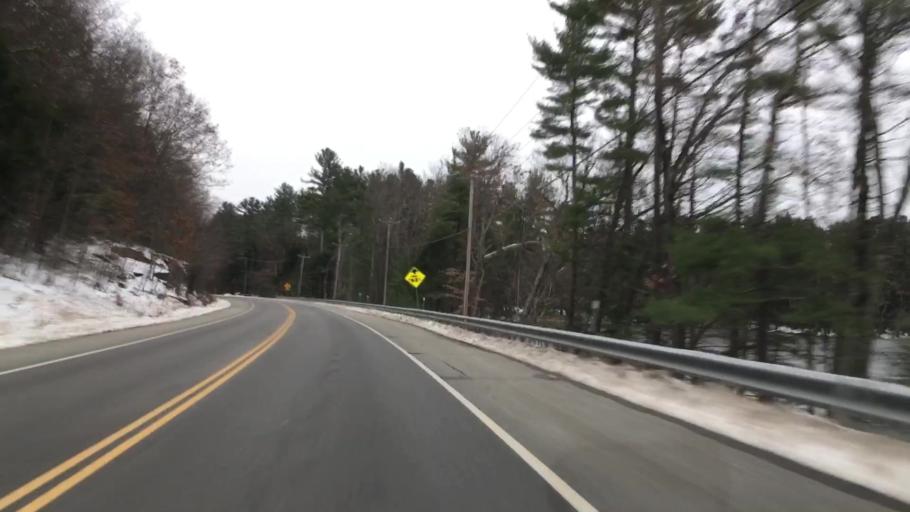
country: US
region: New Hampshire
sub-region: Hillsborough County
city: Milford
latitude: 42.8857
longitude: -71.6080
